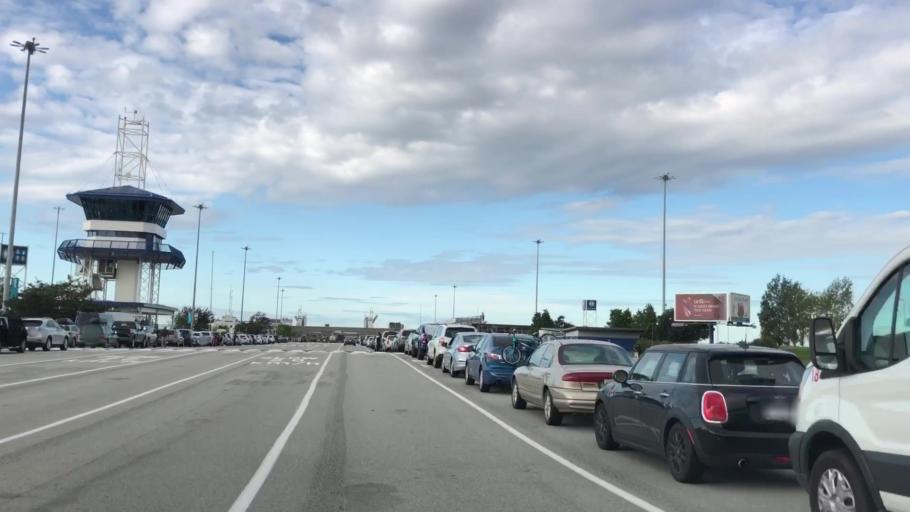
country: US
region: Washington
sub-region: Whatcom County
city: Point Roberts
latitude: 49.0100
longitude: -123.1272
